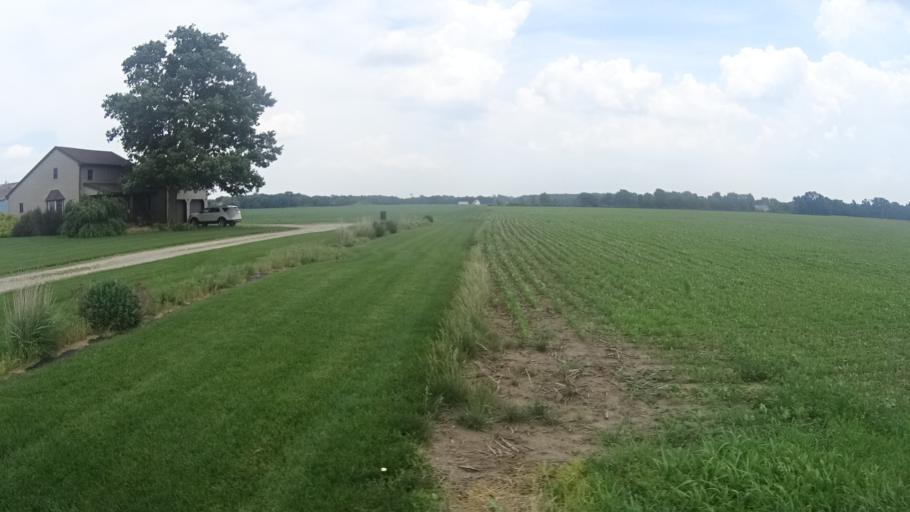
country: US
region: Ohio
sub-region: Huron County
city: Monroeville
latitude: 41.2953
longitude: -82.6718
